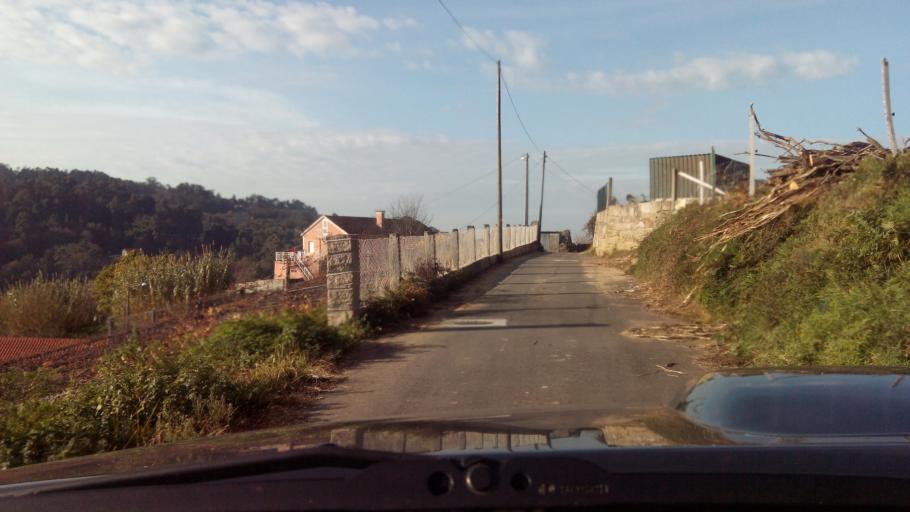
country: ES
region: Galicia
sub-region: Provincia de Pontevedra
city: Marin
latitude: 42.3639
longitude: -8.7140
